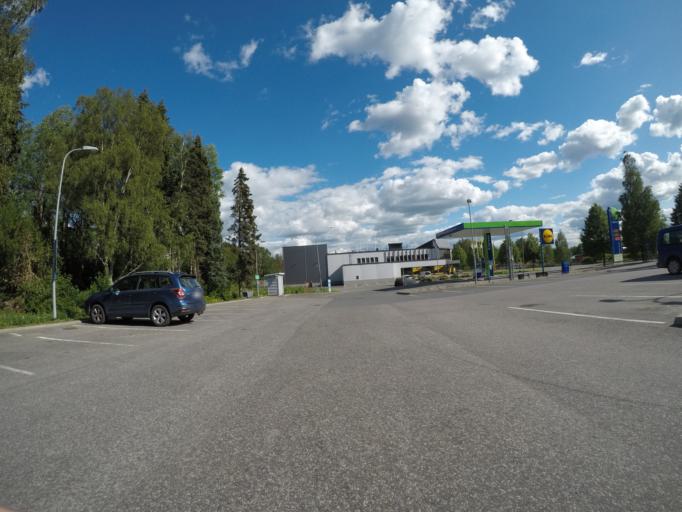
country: FI
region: Haeme
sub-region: Haemeenlinna
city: Haemeenlinna
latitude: 61.0012
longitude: 24.4876
